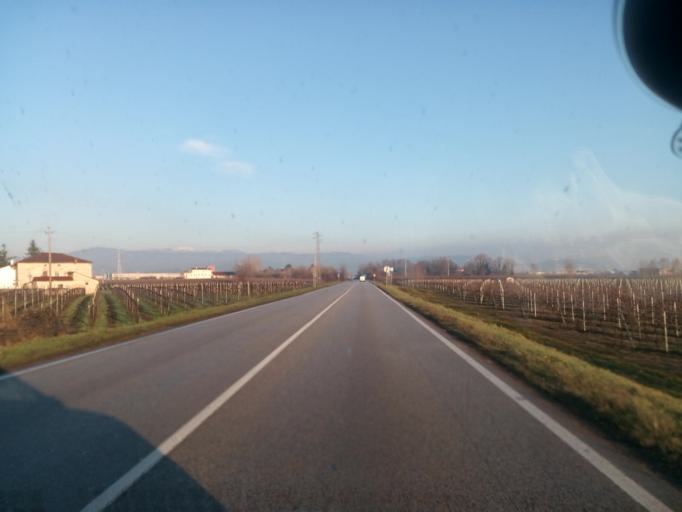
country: IT
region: Veneto
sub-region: Provincia di Vicenza
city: Monticello di Fara
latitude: 45.4235
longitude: 11.3756
